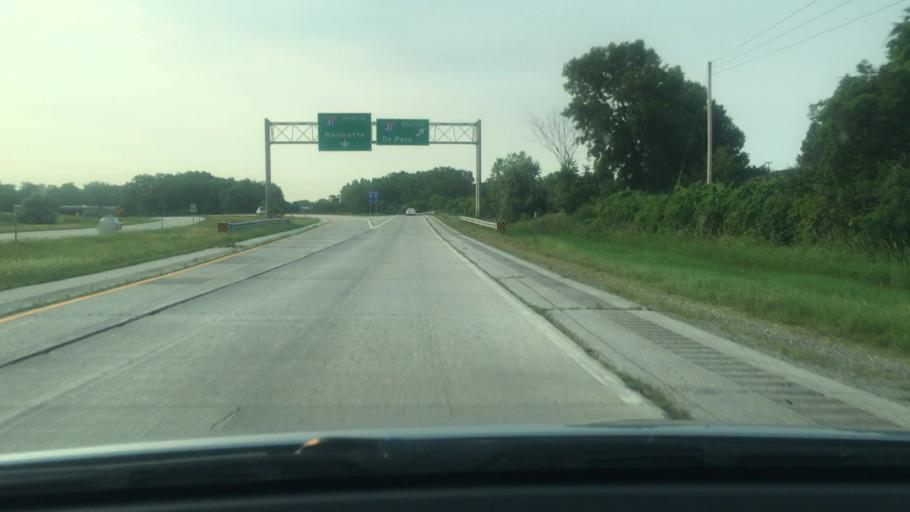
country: US
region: Wisconsin
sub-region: Brown County
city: Ashwaubenon
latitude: 44.4863
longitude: -88.0863
